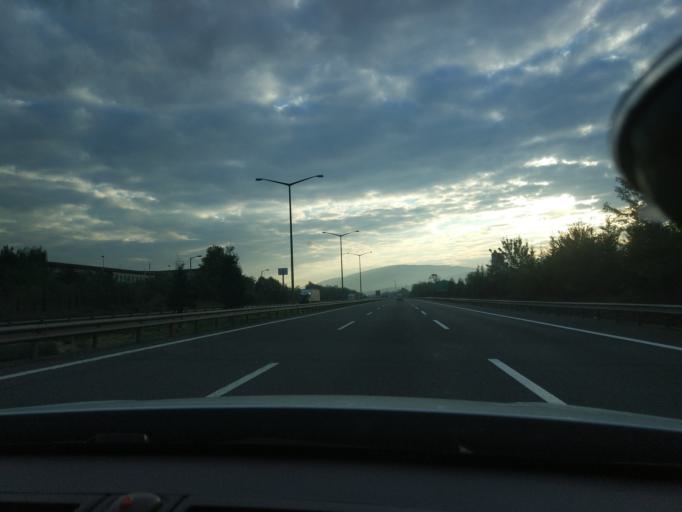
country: TR
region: Sakarya
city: Hendek
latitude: 40.7540
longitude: 30.7259
